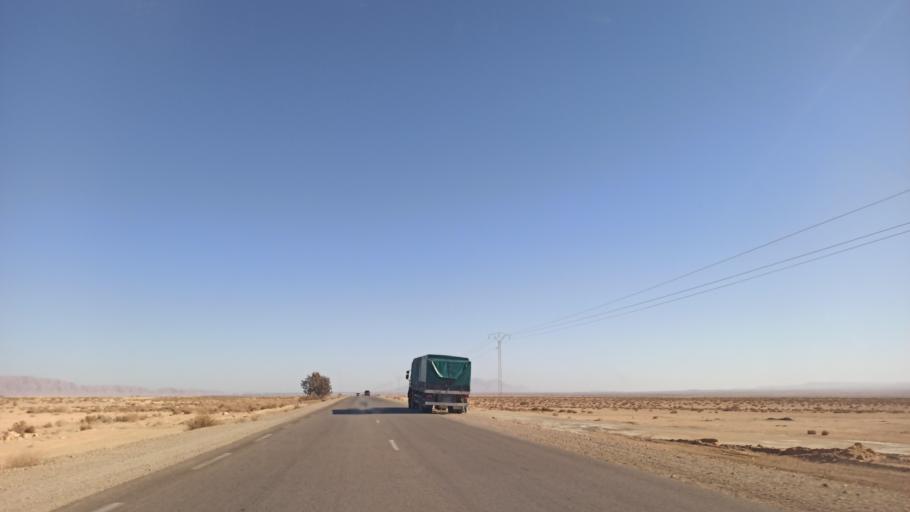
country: TN
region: Gafsa
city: Al Metlaoui
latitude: 34.3215
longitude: 8.5225
